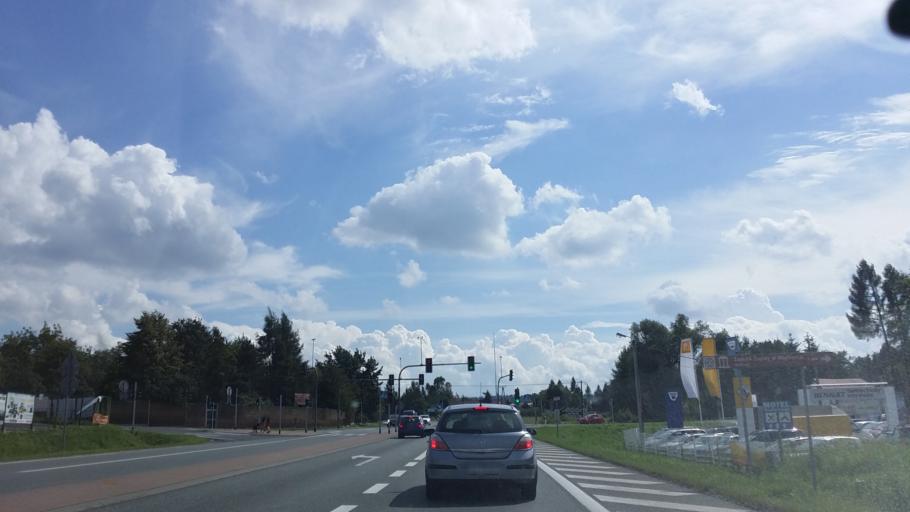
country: PL
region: Lesser Poland Voivodeship
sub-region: Powiat wielicki
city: Wieliczka
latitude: 49.9907
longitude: 20.0807
